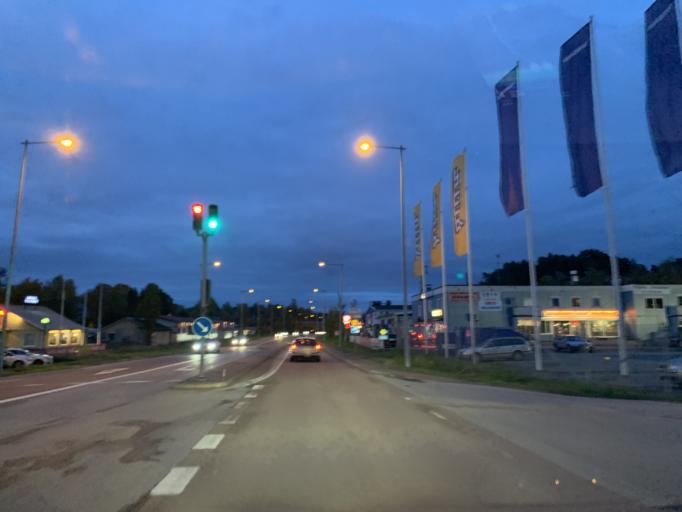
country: SE
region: Stockholm
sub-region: Botkyrka Kommun
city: Tumba
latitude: 59.1903
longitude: 17.8221
